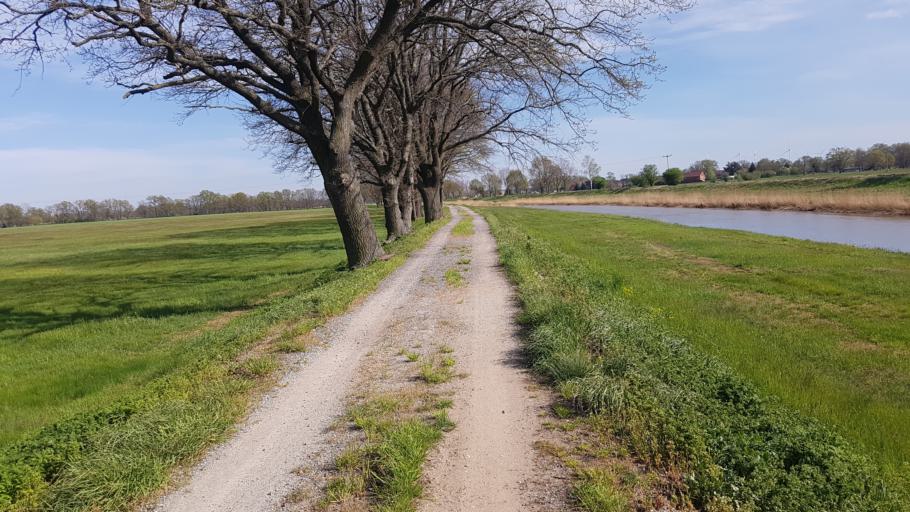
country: DE
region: Brandenburg
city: Falkenberg
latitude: 51.6203
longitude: 13.2892
